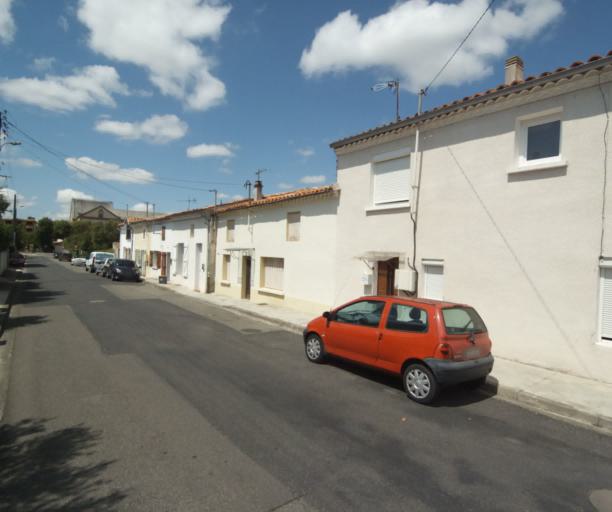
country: FR
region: Midi-Pyrenees
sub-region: Departement de la Haute-Garonne
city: Revel
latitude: 43.4550
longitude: 2.0061
